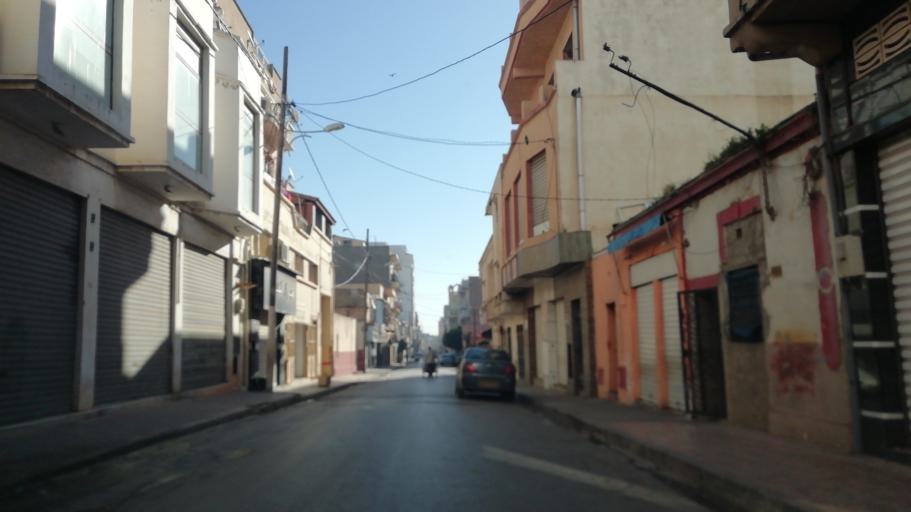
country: DZ
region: Oran
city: Oran
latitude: 35.6818
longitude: -0.6573
